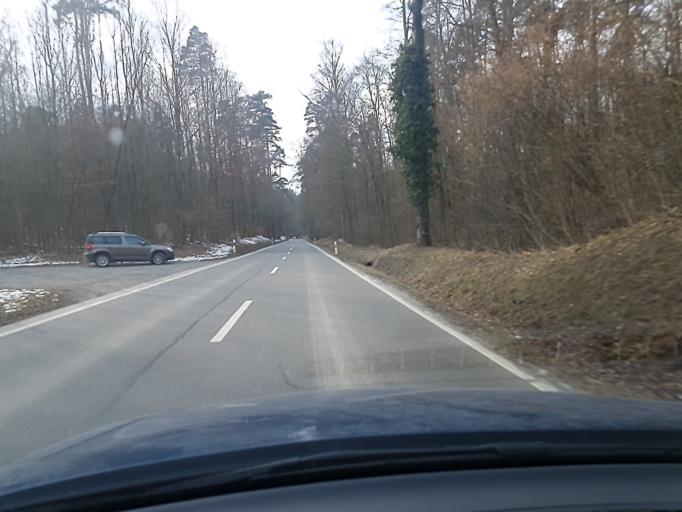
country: DE
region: Baden-Wuerttemberg
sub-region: Regierungsbezirk Stuttgart
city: Eberdingen
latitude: 48.8657
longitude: 8.9806
